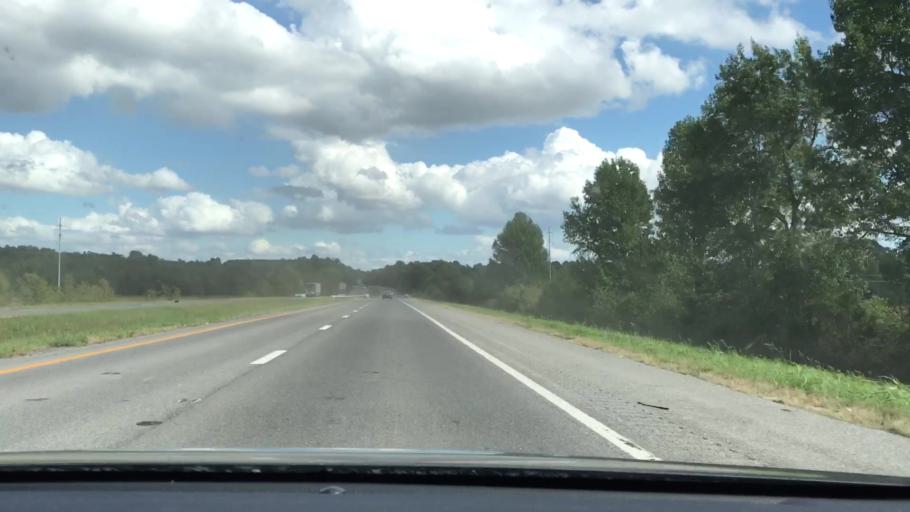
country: US
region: Kentucky
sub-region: Graves County
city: Mayfield
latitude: 36.7693
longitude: -88.6263
